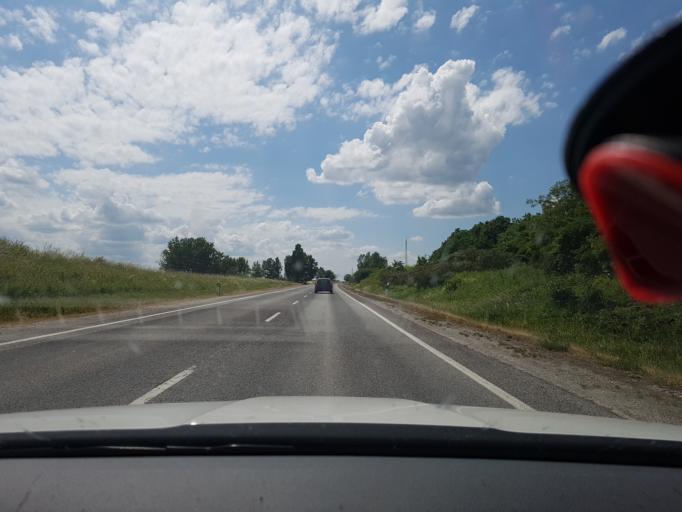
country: HU
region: Heves
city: Domoszlo
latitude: 47.7456
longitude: 20.1464
